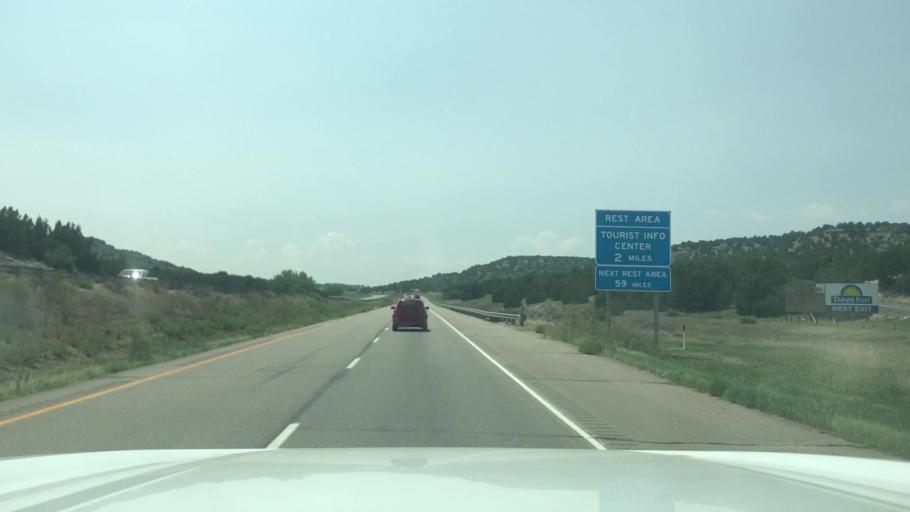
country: US
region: Colorado
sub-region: Pueblo County
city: Colorado City
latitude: 37.9874
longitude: -104.7707
